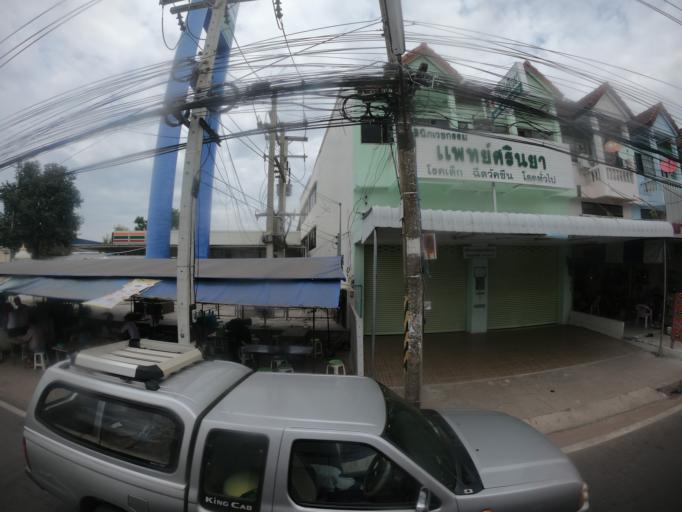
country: TH
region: Maha Sarakham
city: Maha Sarakham
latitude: 16.1784
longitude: 103.3118
